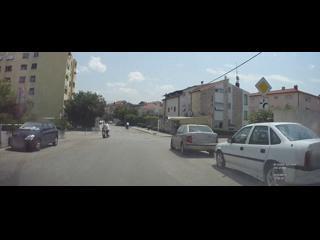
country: HR
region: Splitsko-Dalmatinska
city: Vranjic
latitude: 43.5229
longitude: 16.4740
